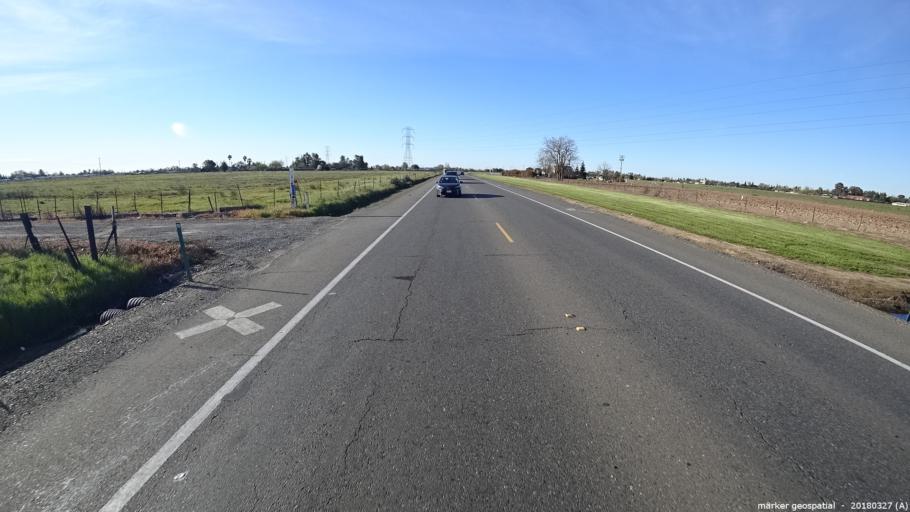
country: US
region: California
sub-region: Sacramento County
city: Florin
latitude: 38.5035
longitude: -121.3722
